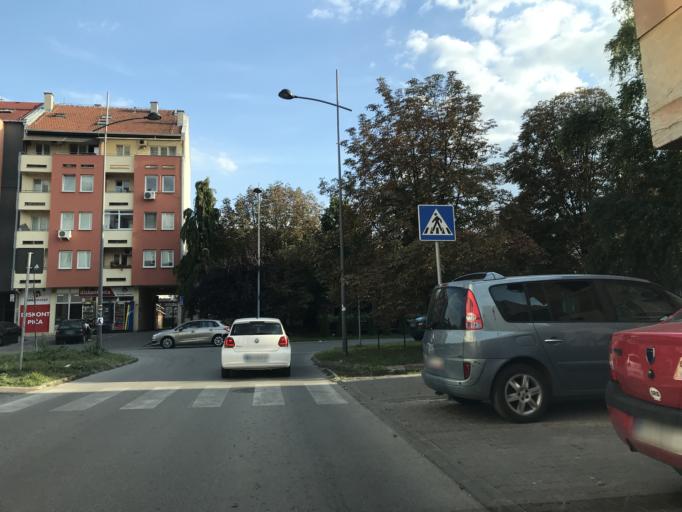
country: RS
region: Autonomna Pokrajina Vojvodina
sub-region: Juznobacki Okrug
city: Novi Sad
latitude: 45.2526
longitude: 19.8308
